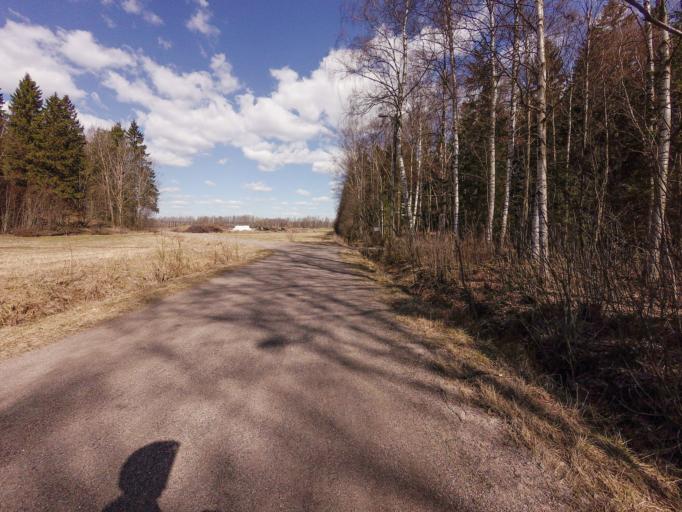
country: FI
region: Uusimaa
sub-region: Helsinki
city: Vantaa
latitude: 60.2163
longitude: 25.0327
